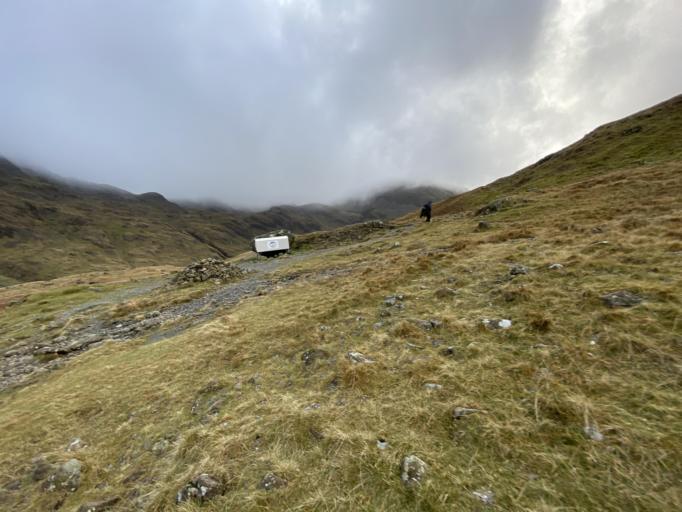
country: GB
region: England
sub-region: Cumbria
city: Keswick
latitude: 54.4751
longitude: -3.2068
